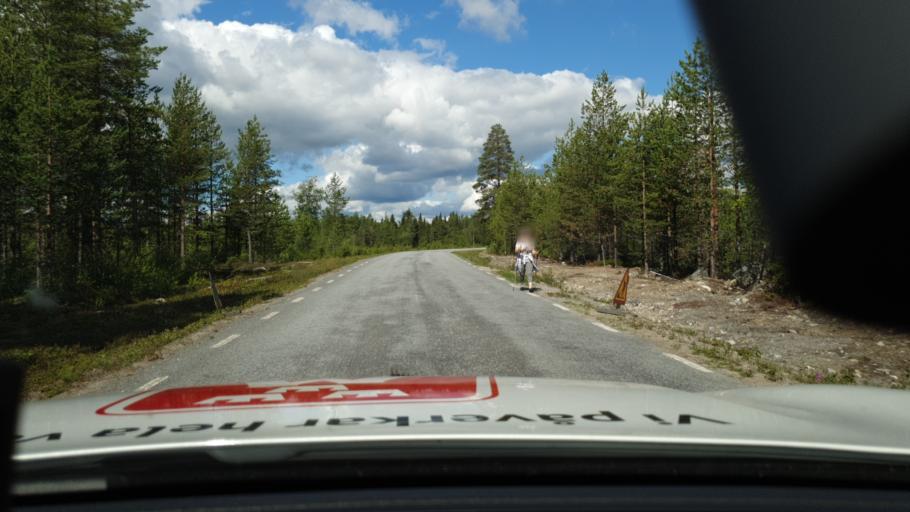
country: SE
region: Norrbotten
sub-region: Lulea Kommun
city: Ranea
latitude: 65.8327
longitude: 22.3116
